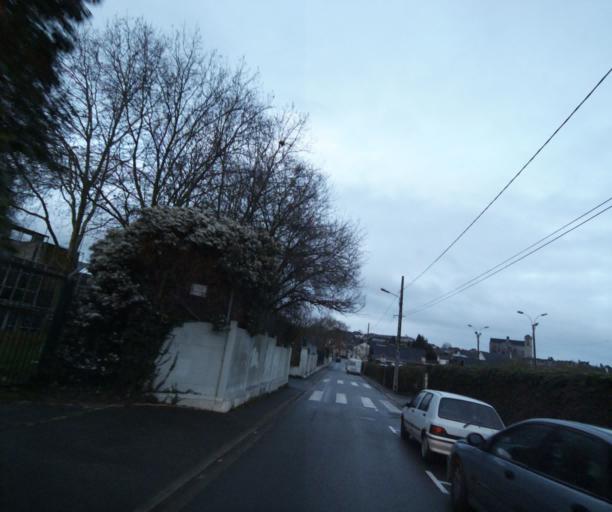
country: FR
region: Pays de la Loire
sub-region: Departement de la Sarthe
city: Coulaines
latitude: 48.0143
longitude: 0.1920
